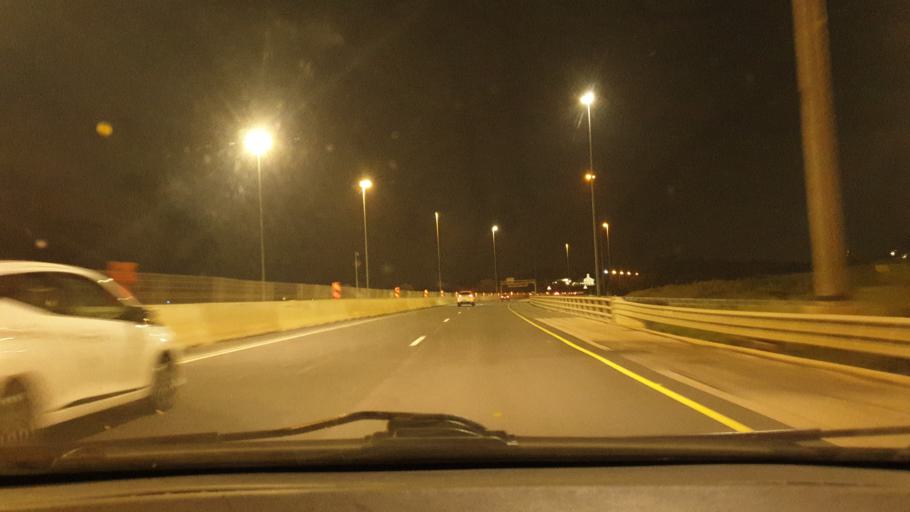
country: IL
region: Central District
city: Ramla
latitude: 31.9214
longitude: 34.8384
